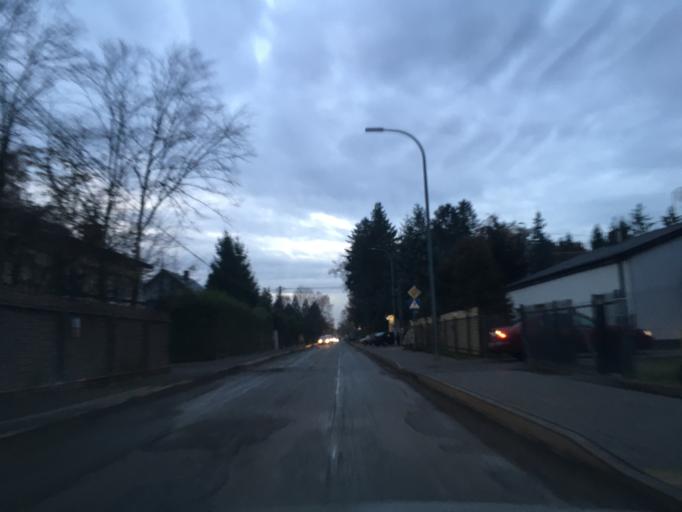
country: PL
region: Masovian Voivodeship
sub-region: Powiat piaseczynski
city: Piaseczno
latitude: 52.0542
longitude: 20.9851
